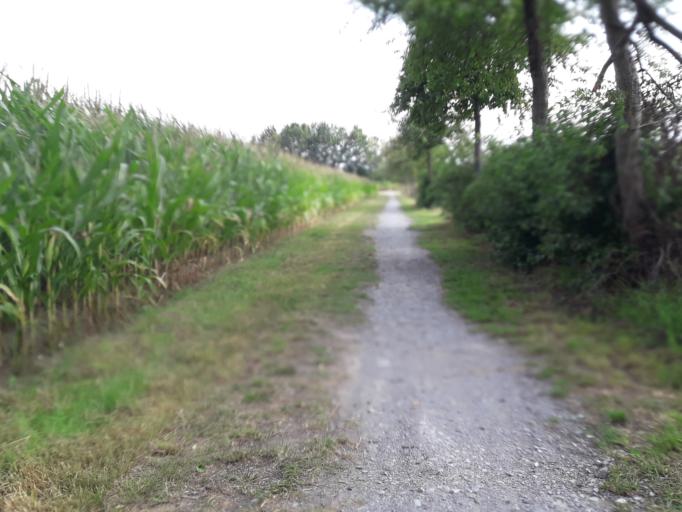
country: DE
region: North Rhine-Westphalia
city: Bad Lippspringe
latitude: 51.7721
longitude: 8.8121
